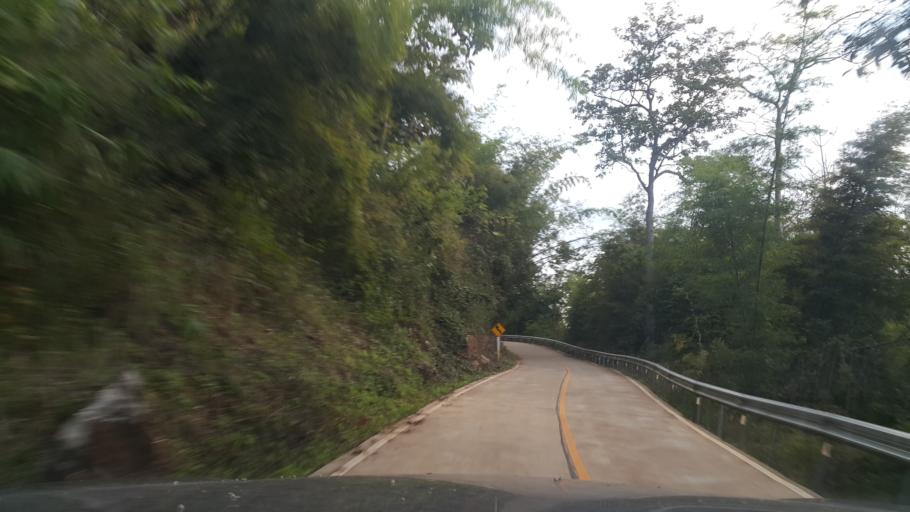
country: TH
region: Chiang Mai
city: Samoeng
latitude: 18.9936
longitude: 98.6742
